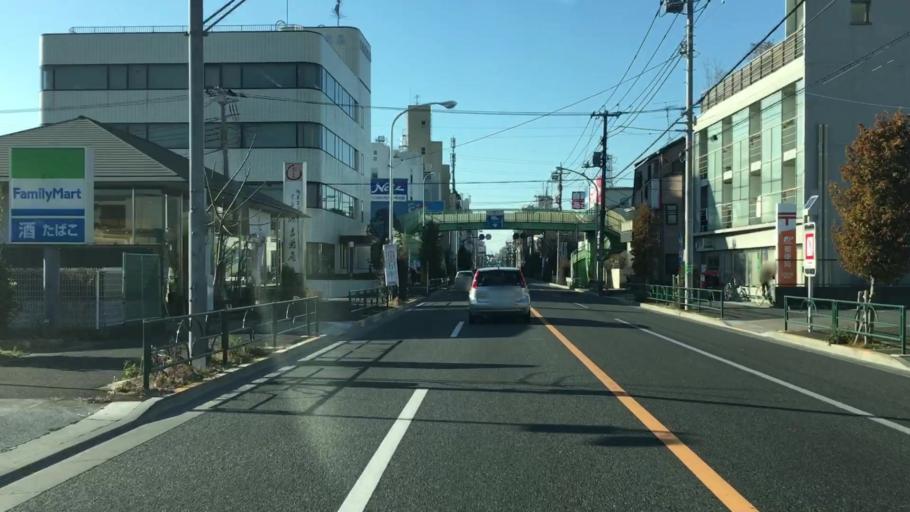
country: JP
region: Tokyo
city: Musashino
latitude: 35.6970
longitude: 139.5936
